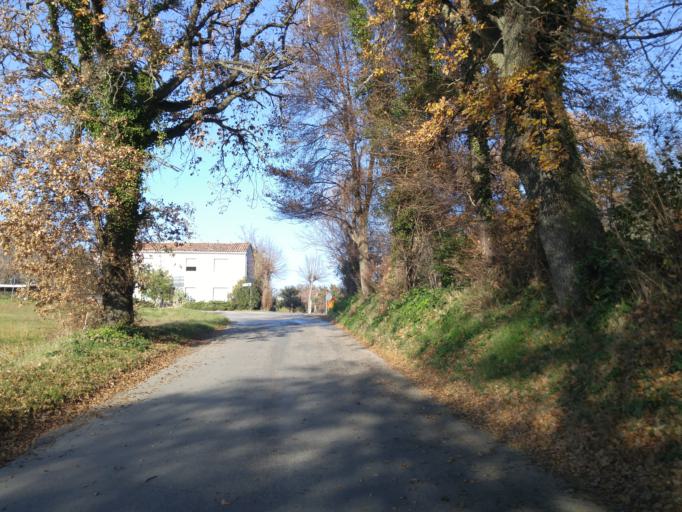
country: IT
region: The Marches
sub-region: Provincia di Pesaro e Urbino
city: Montefelcino
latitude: 43.7274
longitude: 12.8449
